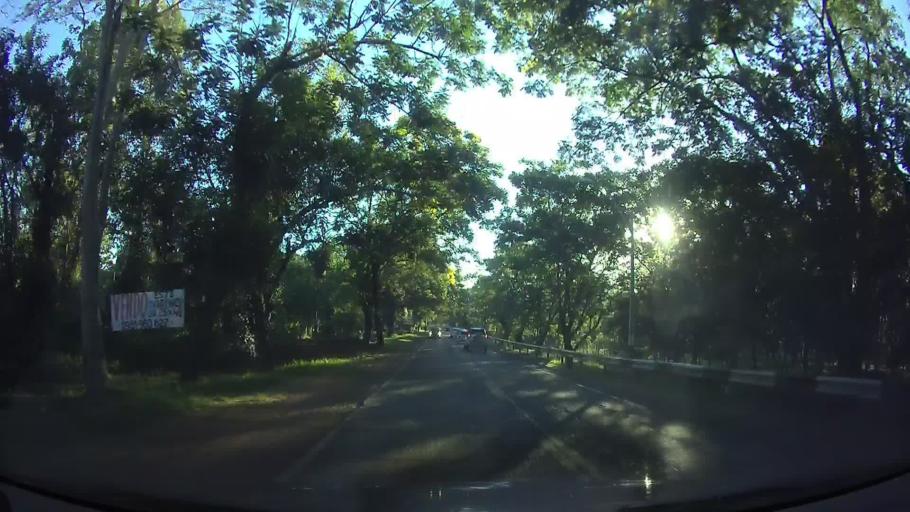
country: PY
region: Central
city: Aregua
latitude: -25.3217
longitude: -57.3905
